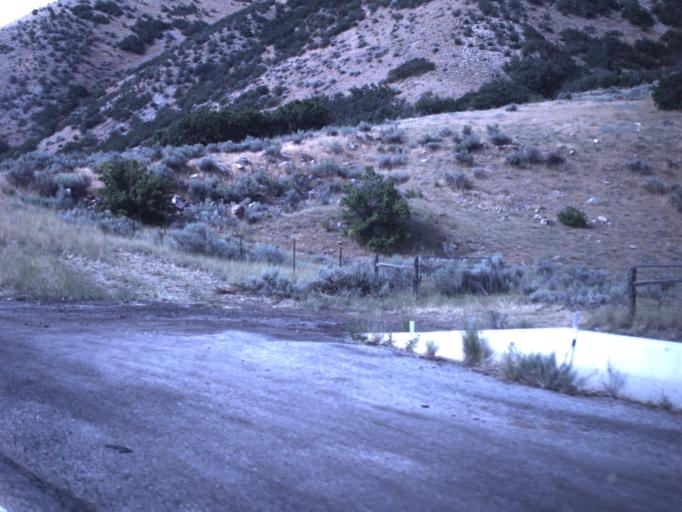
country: US
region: Utah
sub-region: Wasatch County
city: Heber
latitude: 40.4270
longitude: -111.3480
